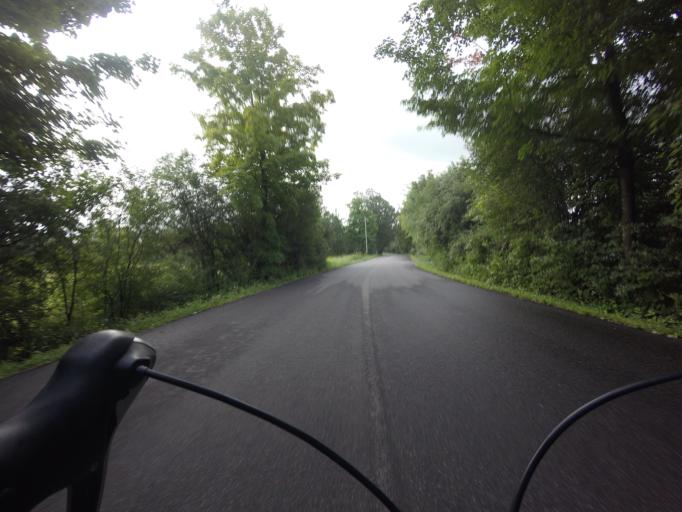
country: CA
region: Ontario
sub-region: Lanark County
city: Smiths Falls
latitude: 44.9567
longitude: -75.7991
